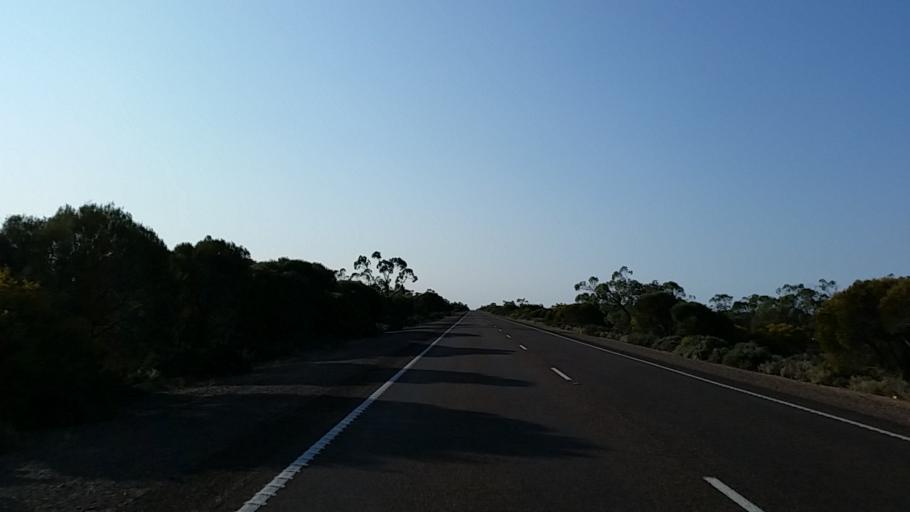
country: AU
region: South Australia
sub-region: Whyalla
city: Whyalla
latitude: -32.7682
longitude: 137.5296
